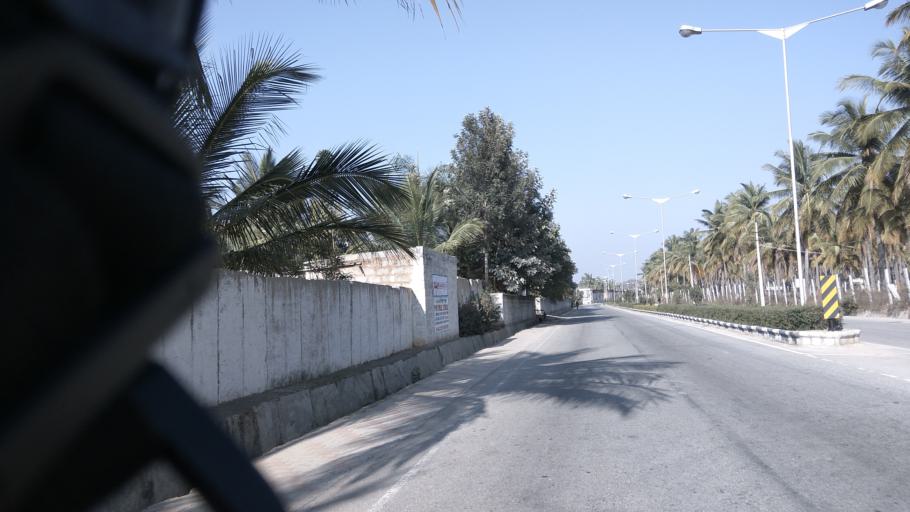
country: IN
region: Karnataka
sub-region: Bangalore Rural
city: Devanhalli
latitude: 13.1986
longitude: 77.6402
